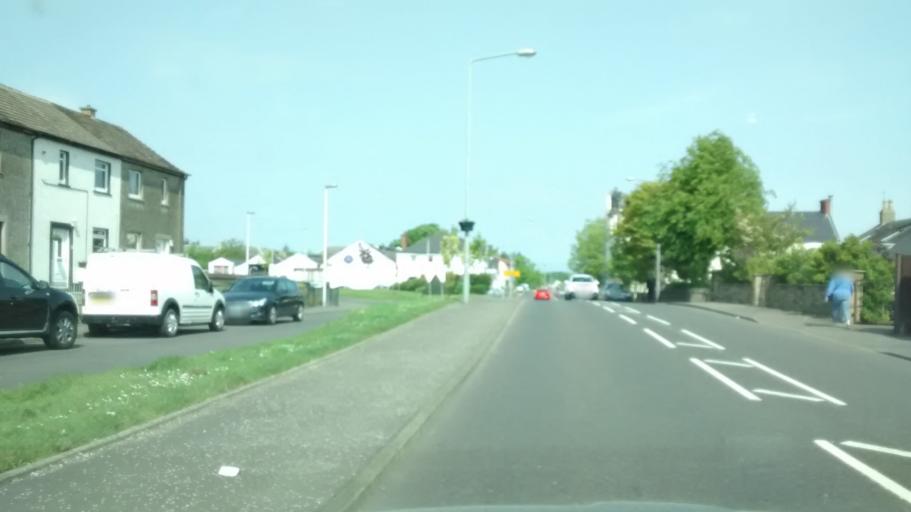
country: GB
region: Scotland
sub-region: West Lothian
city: Mid Calder
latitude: 55.9071
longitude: -3.4928
